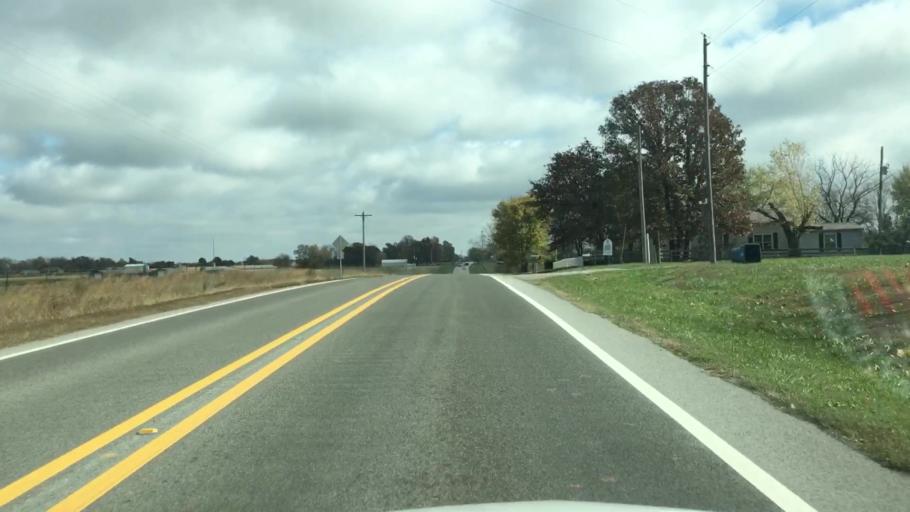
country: US
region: Arkansas
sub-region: Benton County
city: Gentry
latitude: 36.2618
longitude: -94.3668
